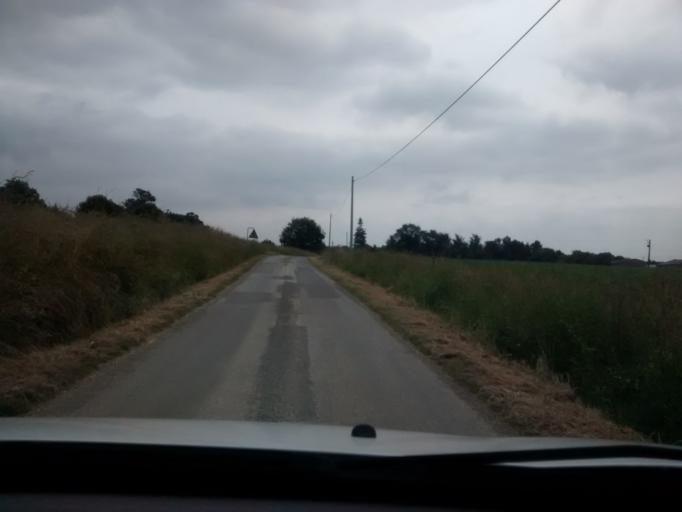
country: FR
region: Brittany
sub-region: Departement d'Ille-et-Vilaine
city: Noyal-sur-Vilaine
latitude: 48.1254
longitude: -1.5070
